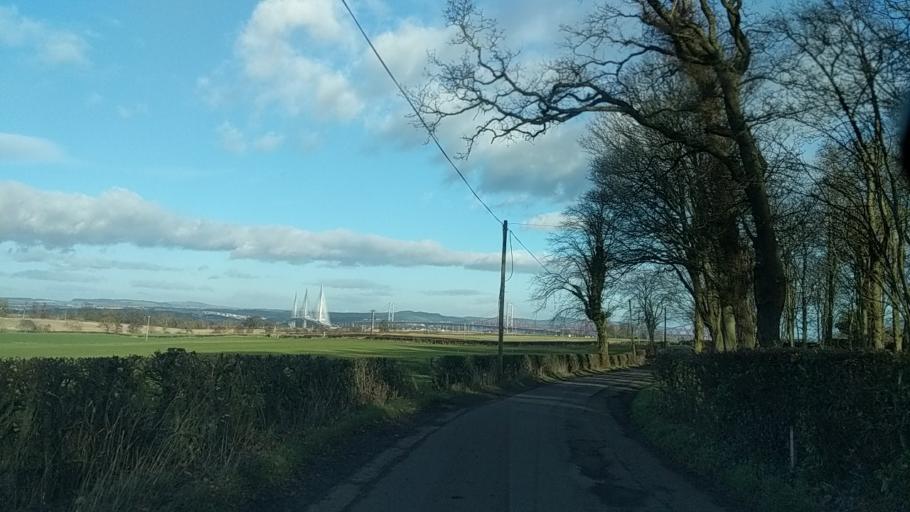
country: GB
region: Scotland
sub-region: Edinburgh
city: Kirkliston
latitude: 55.9761
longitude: -3.4357
